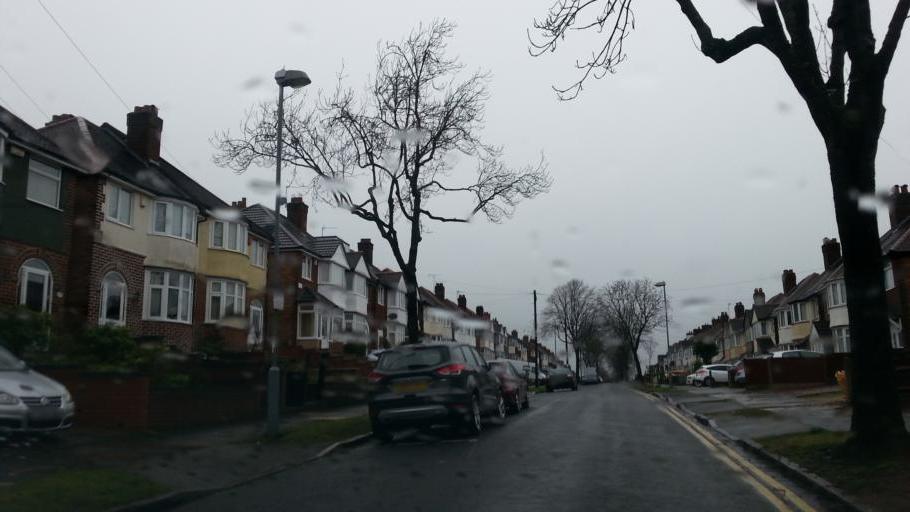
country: GB
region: England
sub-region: City and Borough of Birmingham
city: Hockley
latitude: 52.5397
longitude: -1.9228
